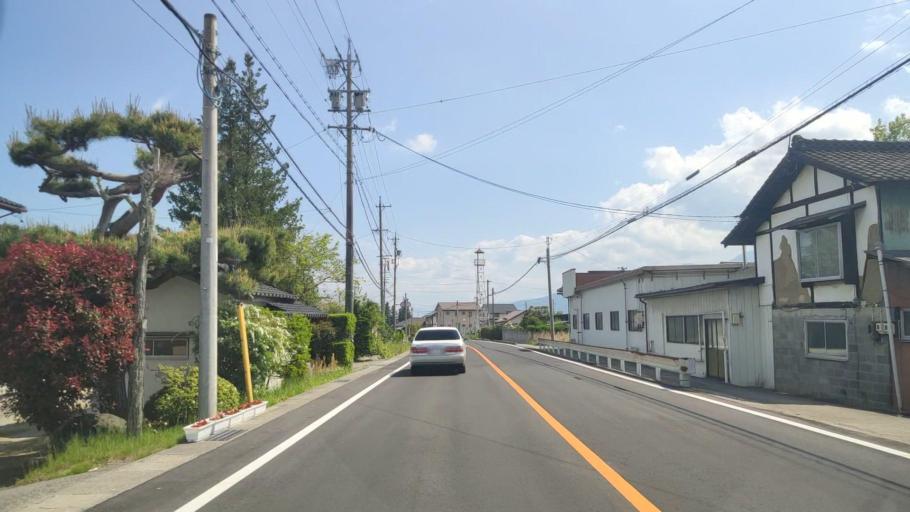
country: JP
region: Nagano
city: Hotaka
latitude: 36.4016
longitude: 137.8614
